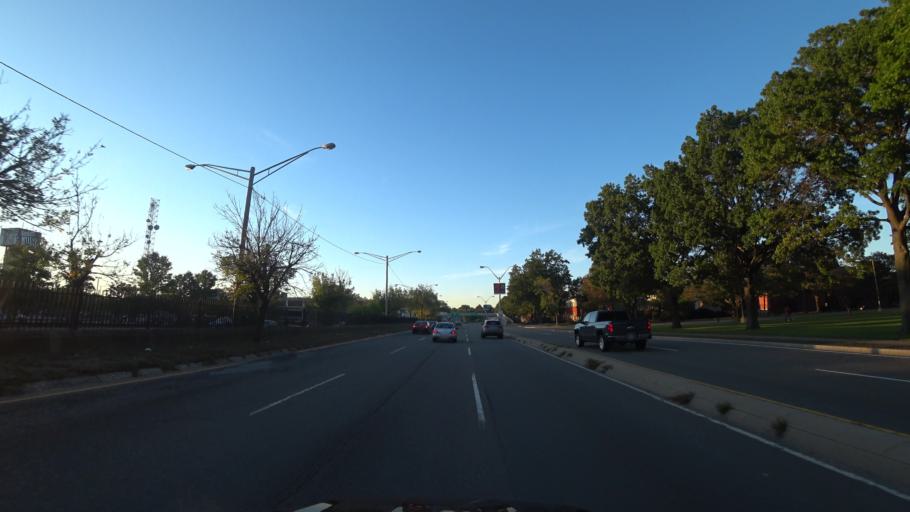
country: US
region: Massachusetts
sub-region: Suffolk County
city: South Boston
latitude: 42.3164
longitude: -71.0483
